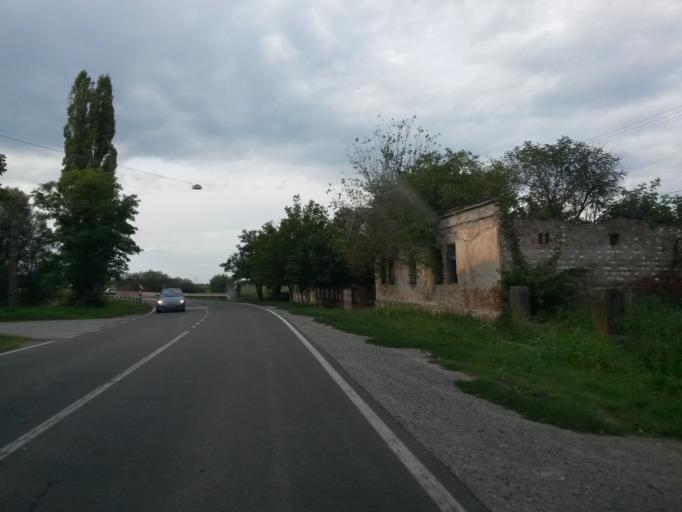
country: HR
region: Osjecko-Baranjska
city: Laslovo
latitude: 45.4087
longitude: 18.6827
